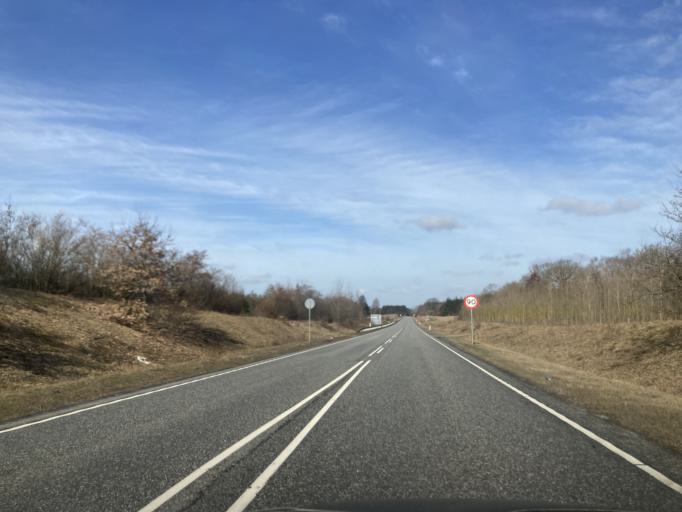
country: DK
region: Central Jutland
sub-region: Hedensted Kommune
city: Torring
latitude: 55.9699
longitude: 9.4015
